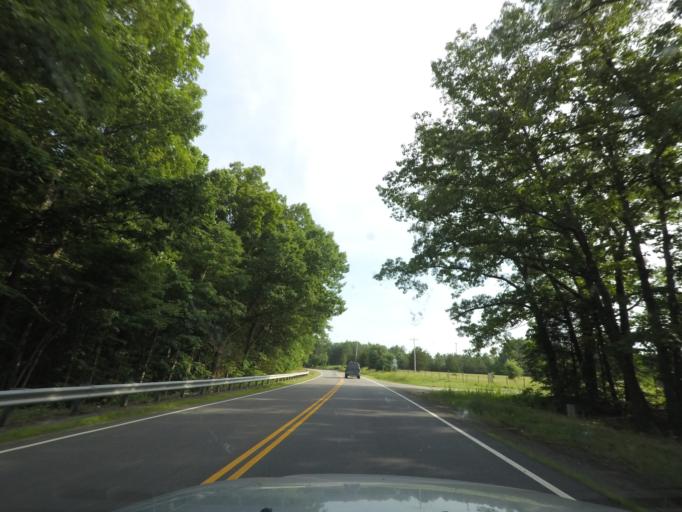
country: US
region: Virginia
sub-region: Mecklenburg County
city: Chase City
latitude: 36.8020
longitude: -78.6044
